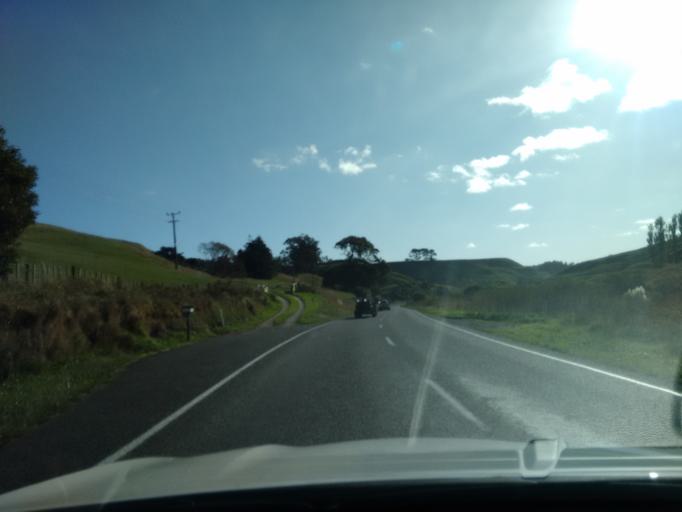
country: NZ
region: Manawatu-Wanganui
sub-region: Wanganui District
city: Wanganui
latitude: -39.8546
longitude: 174.9410
